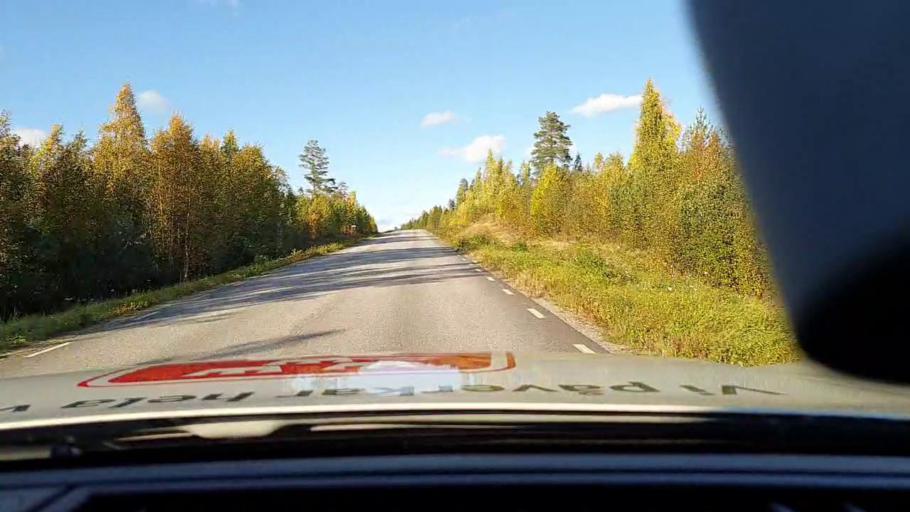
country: SE
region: Norrbotten
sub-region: Pitea Kommun
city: Norrfjarden
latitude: 65.4935
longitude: 21.4738
